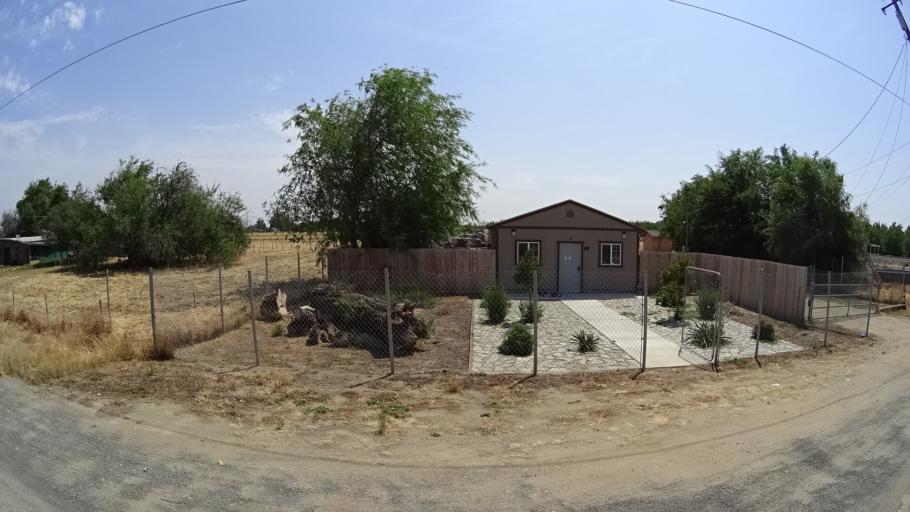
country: US
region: California
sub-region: Kings County
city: Armona
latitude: 36.3105
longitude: -119.7448
